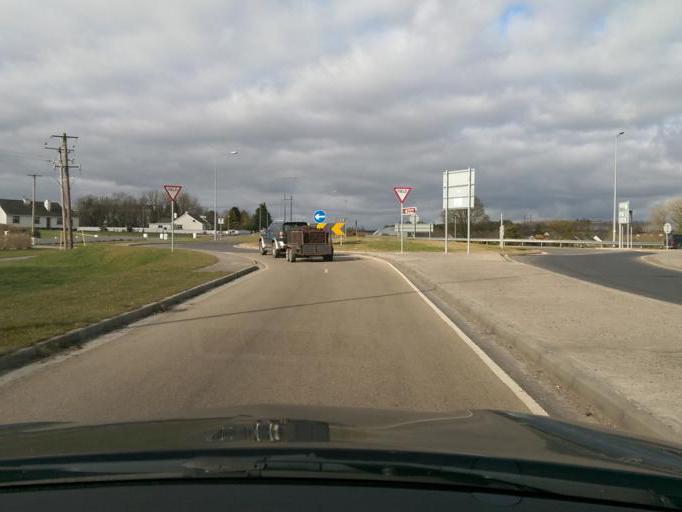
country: IE
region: Leinster
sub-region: An Iarmhi
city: Athlone
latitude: 53.4142
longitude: -7.9848
